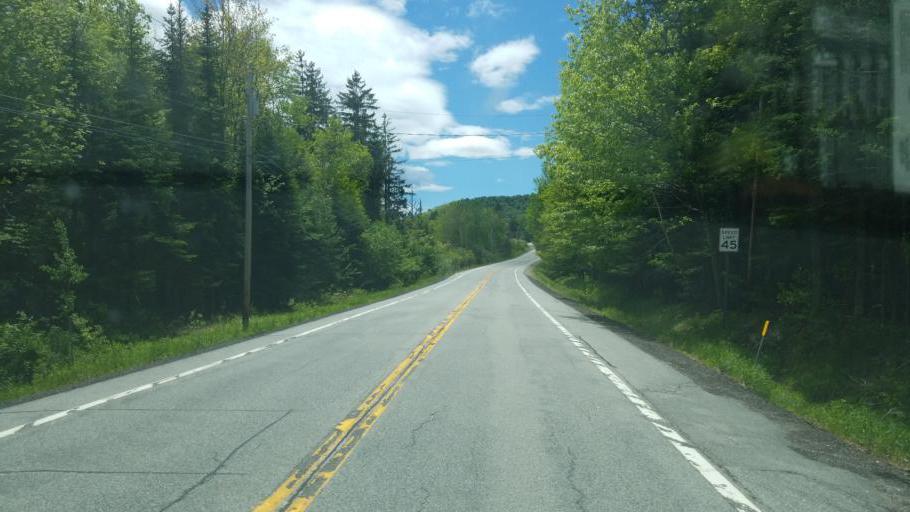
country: US
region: New York
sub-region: Hamilton County
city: Lake Pleasant
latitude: 43.7279
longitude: -74.3062
